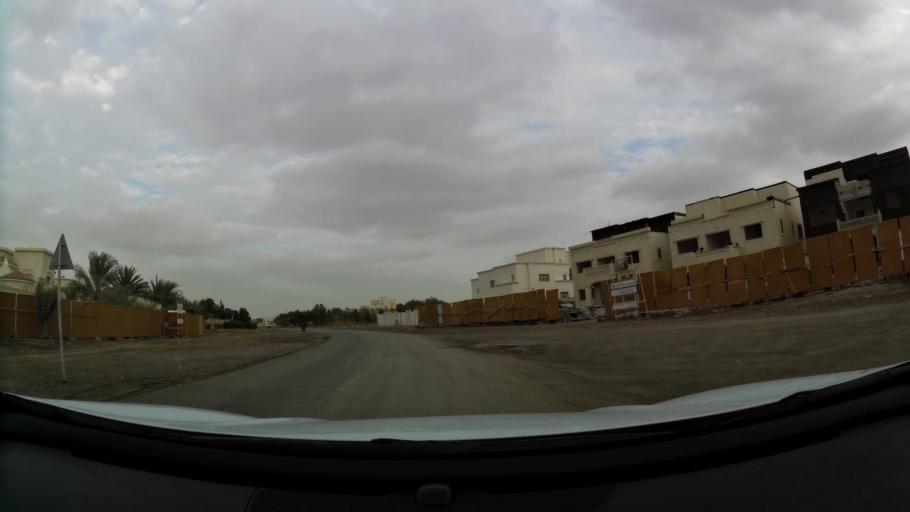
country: AE
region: Abu Dhabi
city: Abu Dhabi
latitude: 24.3528
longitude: 54.5476
